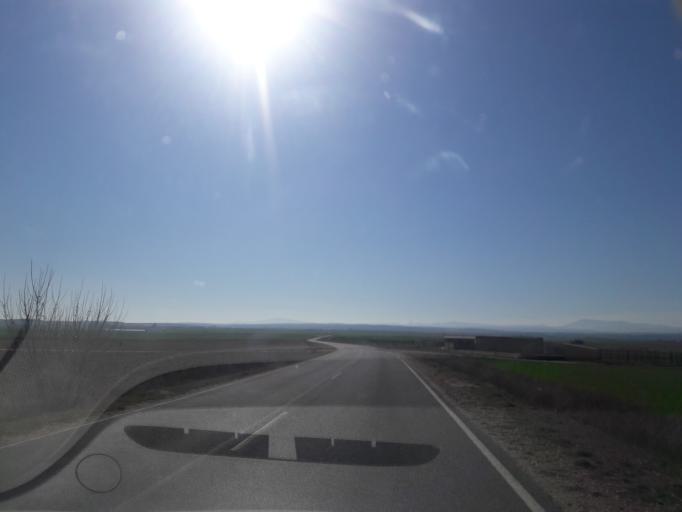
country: ES
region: Castille and Leon
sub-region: Provincia de Salamanca
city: Santiago de la Puebla
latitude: 40.8156
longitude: -5.2592
